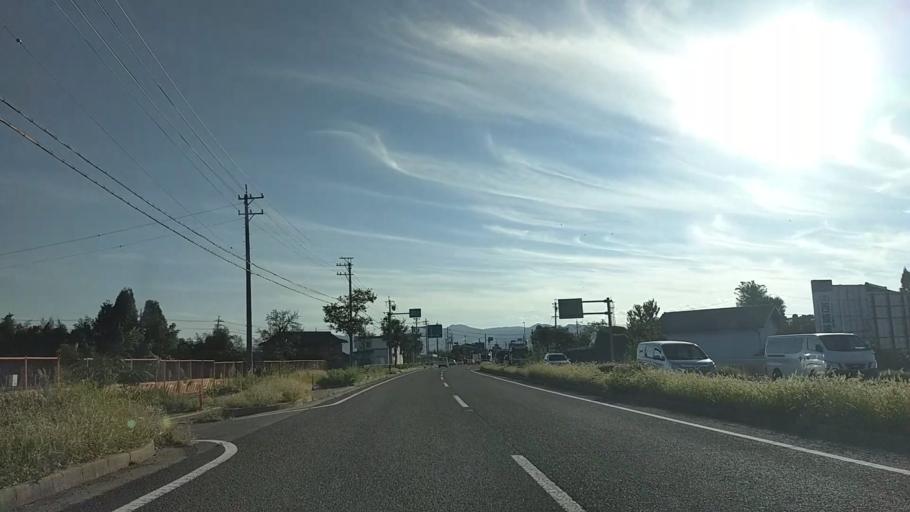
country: JP
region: Nagano
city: Nagano-shi
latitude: 36.5964
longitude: 138.1899
